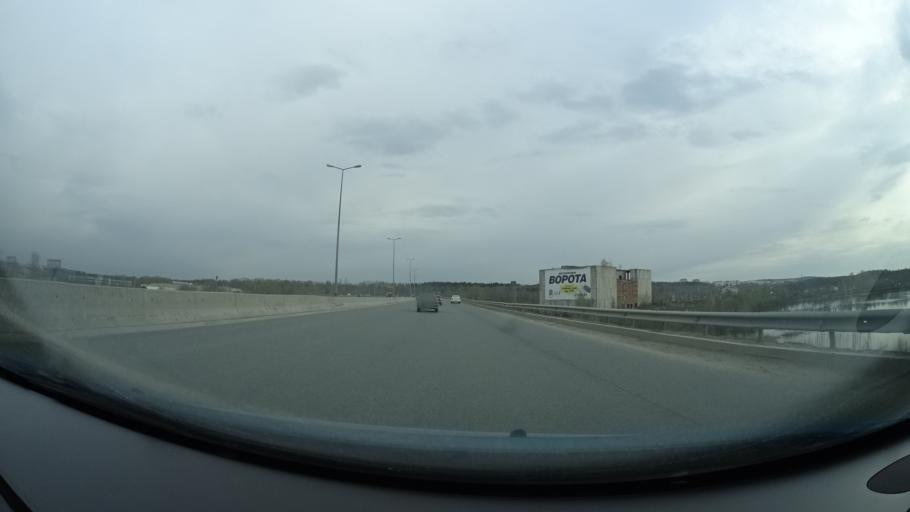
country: RU
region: Perm
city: Kondratovo
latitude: 58.0294
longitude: 56.0558
